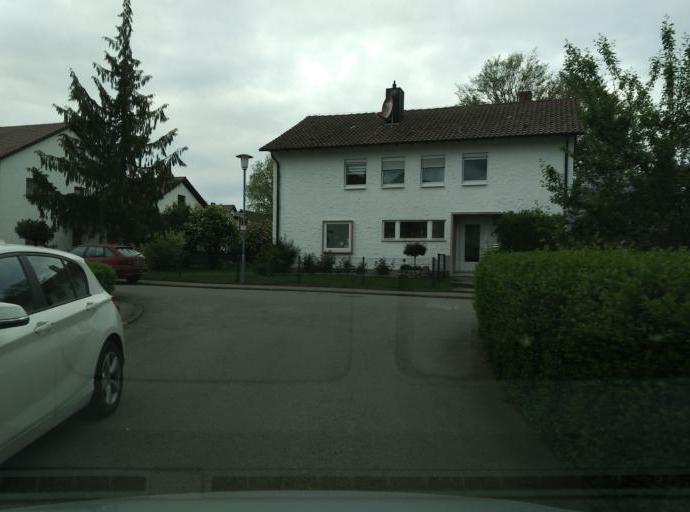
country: DE
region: Baden-Wuerttemberg
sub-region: Regierungsbezirk Stuttgart
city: Neuffen
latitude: 48.5503
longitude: 9.3770
